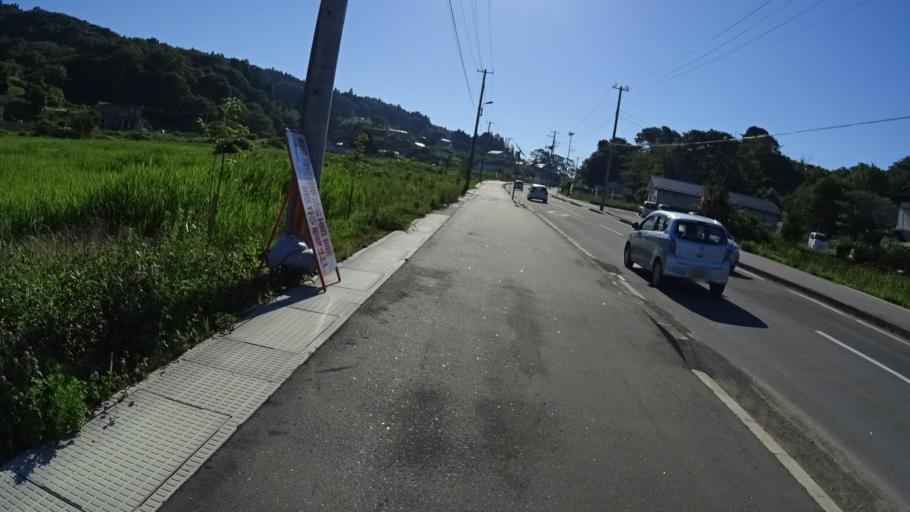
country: JP
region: Iwate
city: Ofunato
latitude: 38.8649
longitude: 141.6146
